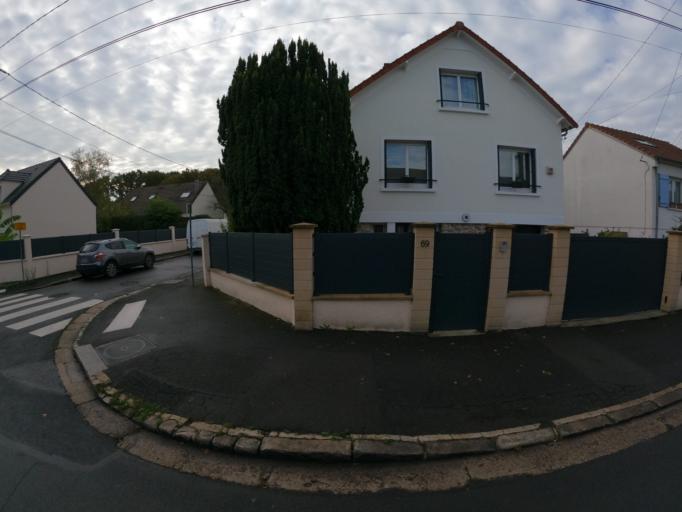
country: FR
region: Ile-de-France
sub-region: Departement de Seine-Saint-Denis
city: Montfermeil
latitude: 48.9000
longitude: 2.5949
